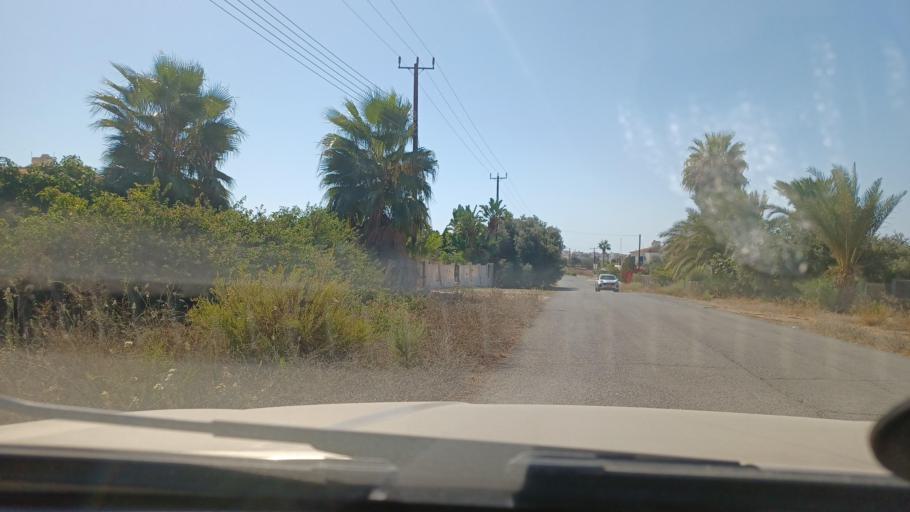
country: CY
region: Pafos
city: Pegeia
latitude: 34.8994
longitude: 32.3330
